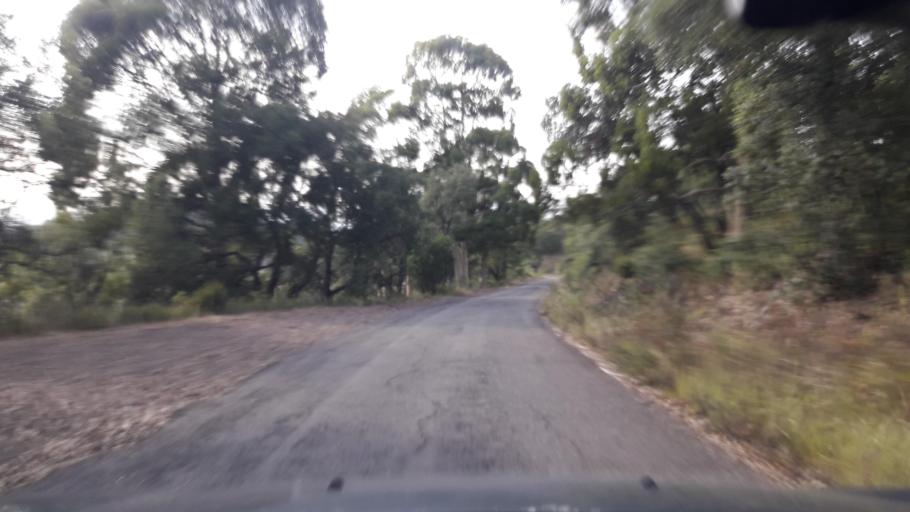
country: FR
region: Provence-Alpes-Cote d'Azur
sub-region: Departement du Var
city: Saint-Raphael
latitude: 43.4990
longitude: 6.7988
